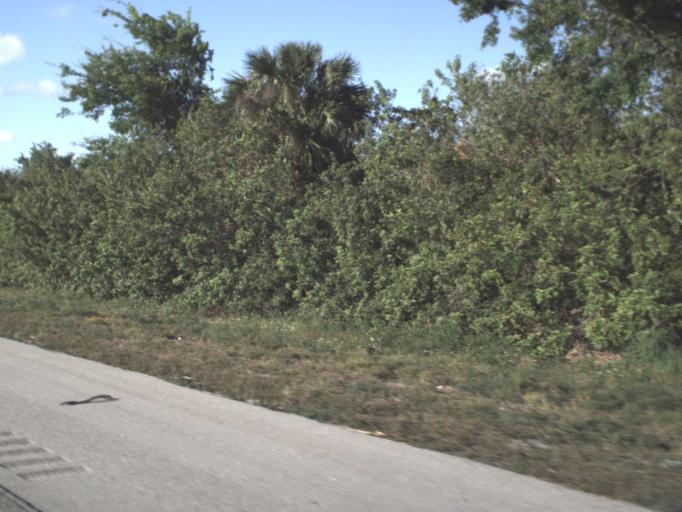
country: US
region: Florida
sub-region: Brevard County
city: Rockledge
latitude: 28.2690
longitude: -80.7296
